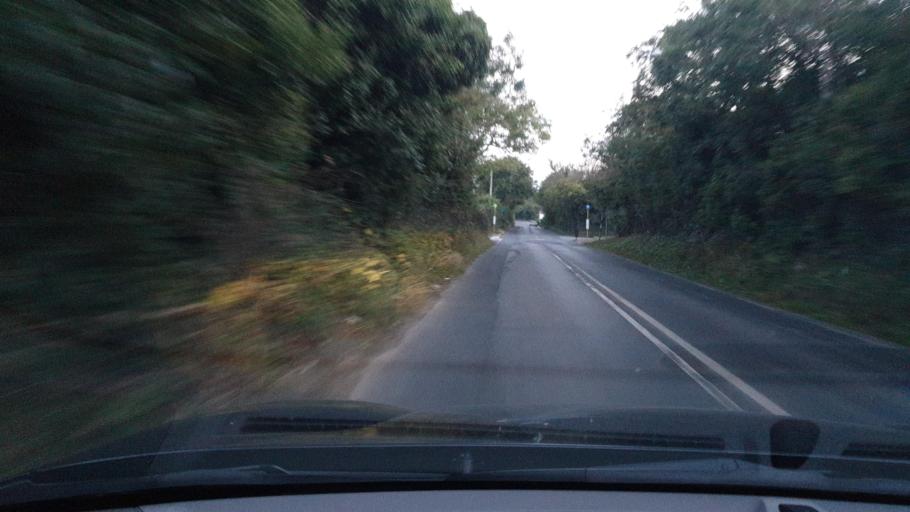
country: IE
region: Leinster
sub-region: Fingal County
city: Skerries
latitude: 53.5549
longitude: -6.1021
